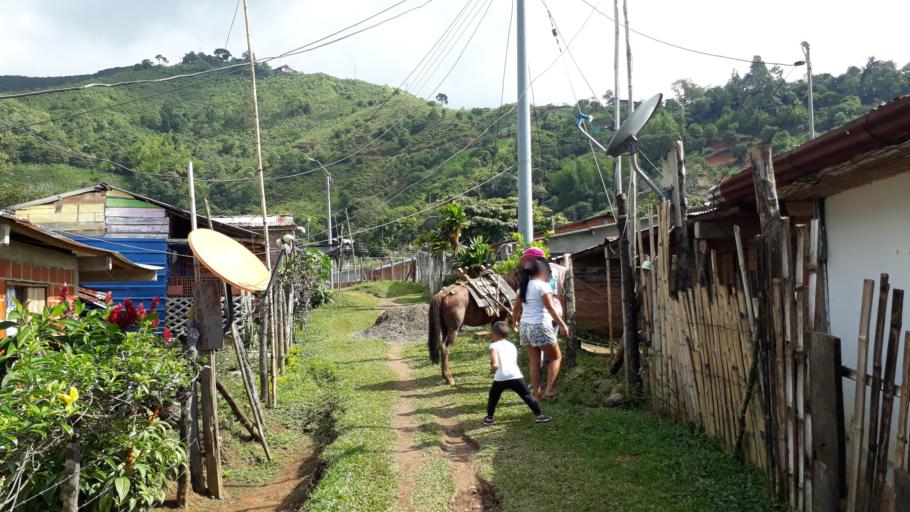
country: CO
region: Valle del Cauca
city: Jamundi
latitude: 3.2669
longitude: -76.6276
